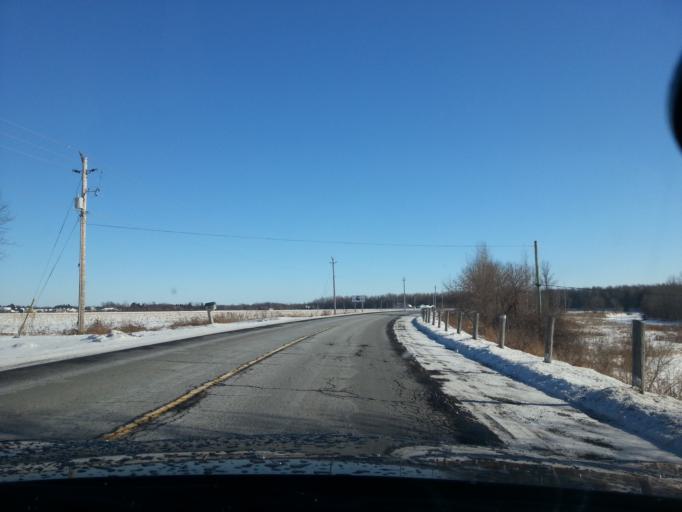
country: CA
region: Ontario
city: Bourget
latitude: 45.2550
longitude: -75.3925
